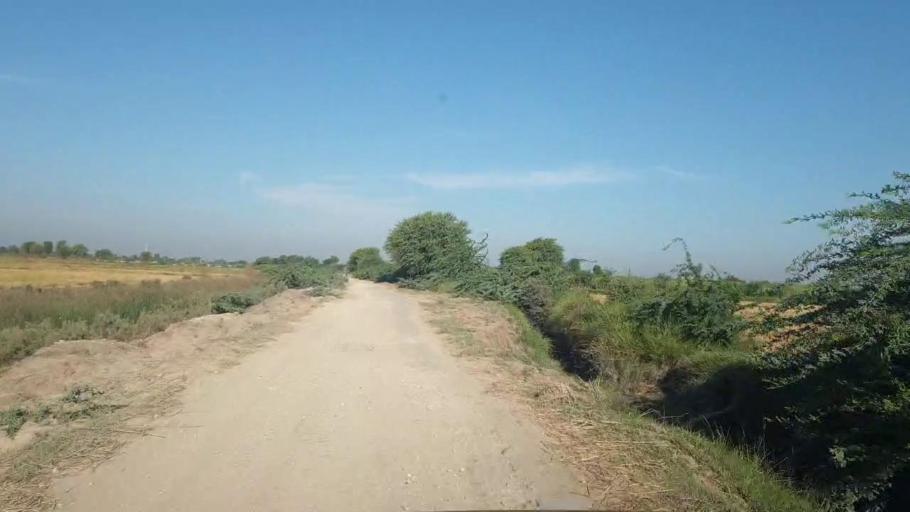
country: PK
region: Sindh
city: Talhar
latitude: 24.8253
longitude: 68.8217
